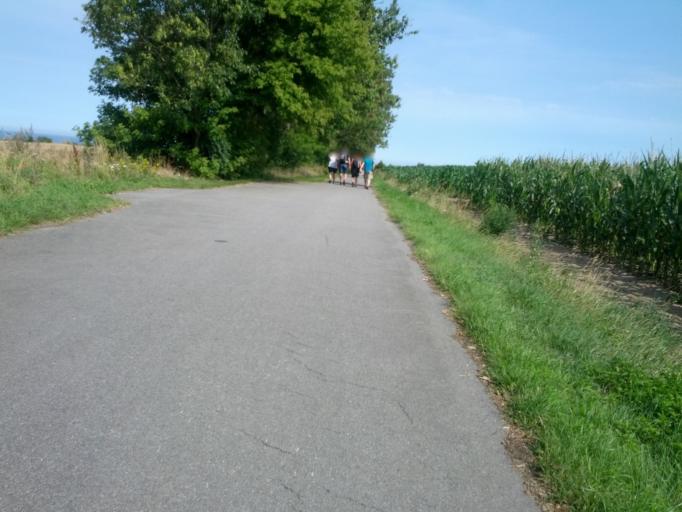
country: DE
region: Mecklenburg-Vorpommern
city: Bastorf
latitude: 54.1263
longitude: 11.6813
